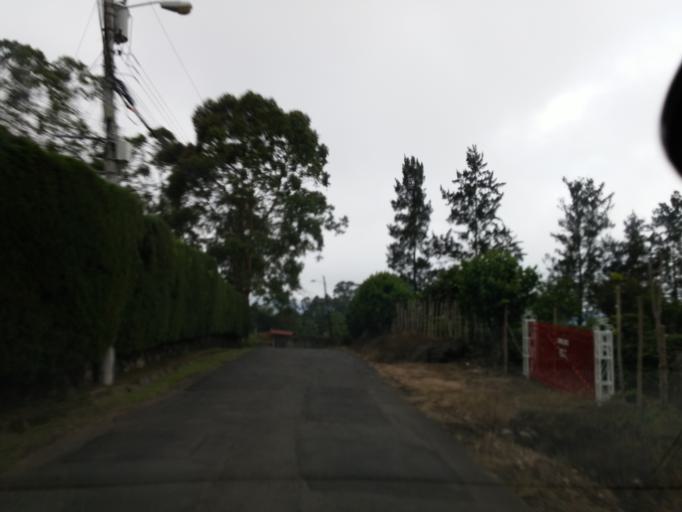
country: CR
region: Heredia
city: San Josecito
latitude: 10.0367
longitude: -84.0980
